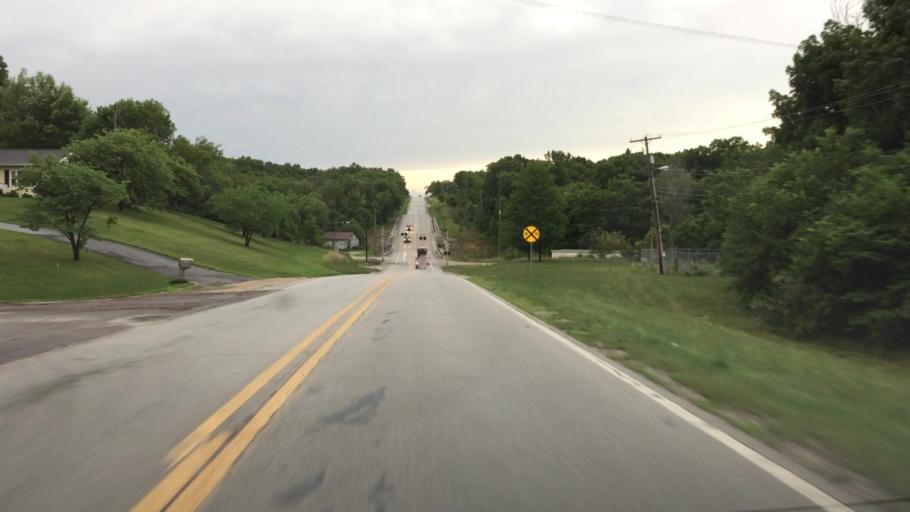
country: US
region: Illinois
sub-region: Hancock County
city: Hamilton
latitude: 40.3883
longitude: -91.3402
